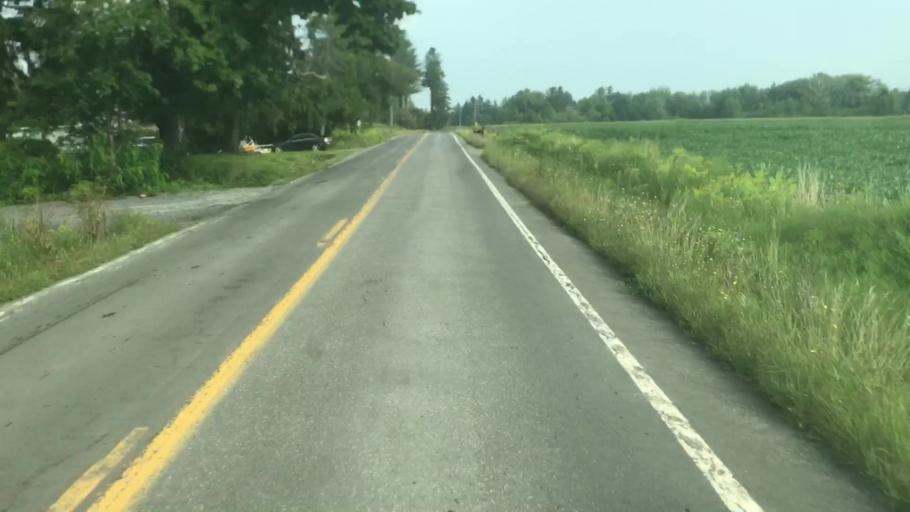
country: US
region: New York
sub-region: Onondaga County
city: Skaneateles
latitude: 42.8968
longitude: -76.4526
